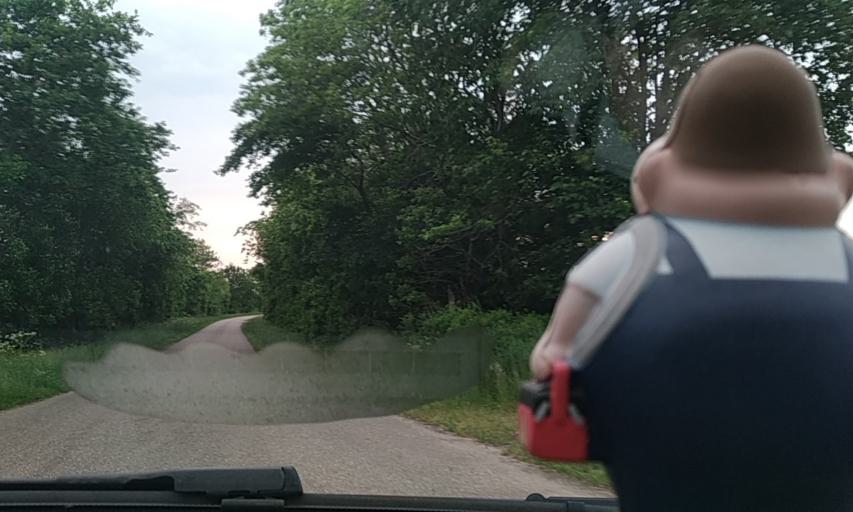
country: DE
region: Schleswig-Holstein
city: Alt Bennebek
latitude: 54.3910
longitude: 9.4089
